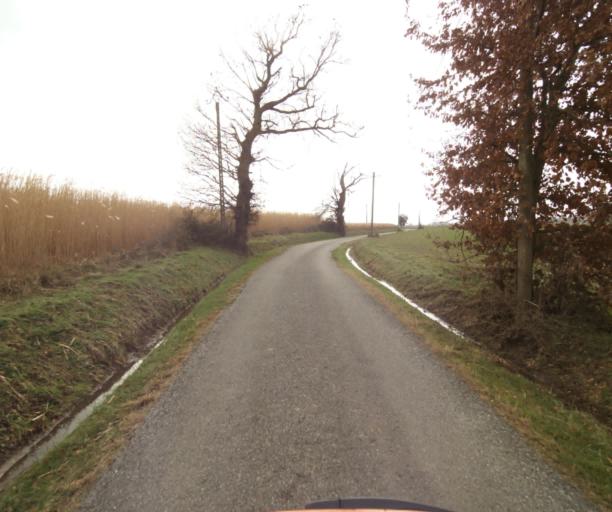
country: FR
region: Midi-Pyrenees
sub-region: Departement de l'Ariege
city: Mazeres
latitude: 43.1868
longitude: 1.6593
